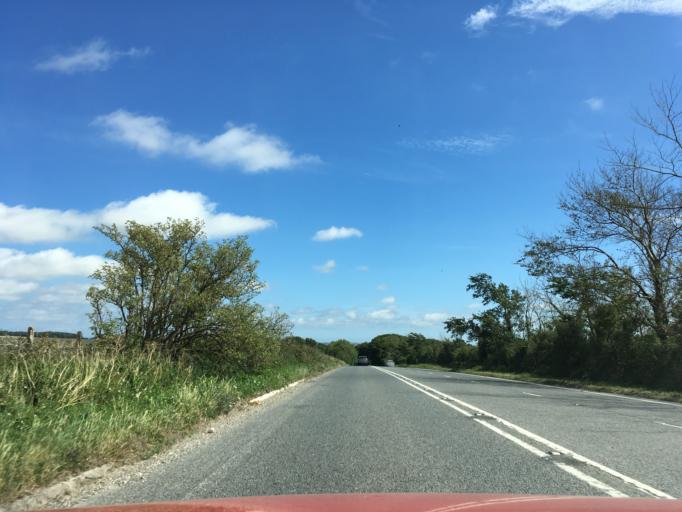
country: GB
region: England
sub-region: Dorset
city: Dorchester
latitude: 50.7686
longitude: -2.5349
